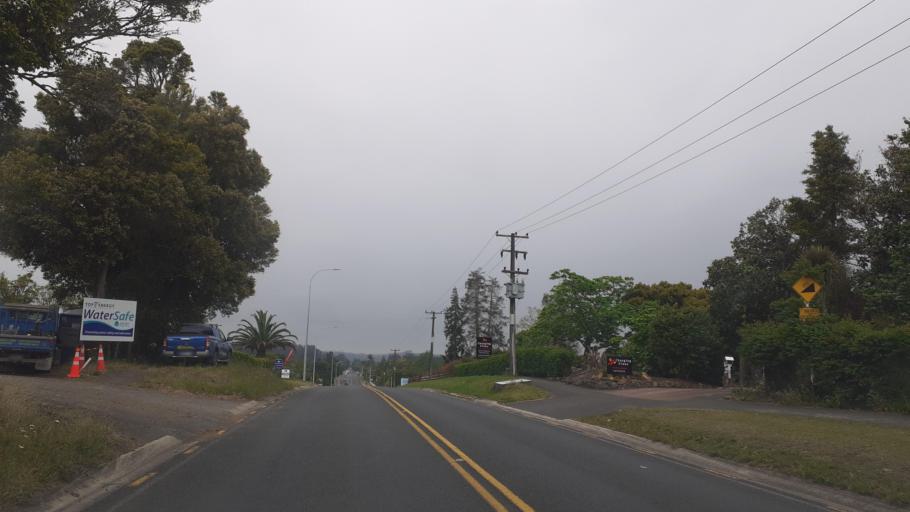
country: NZ
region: Northland
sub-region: Far North District
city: Kerikeri
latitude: -35.2375
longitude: 173.9401
